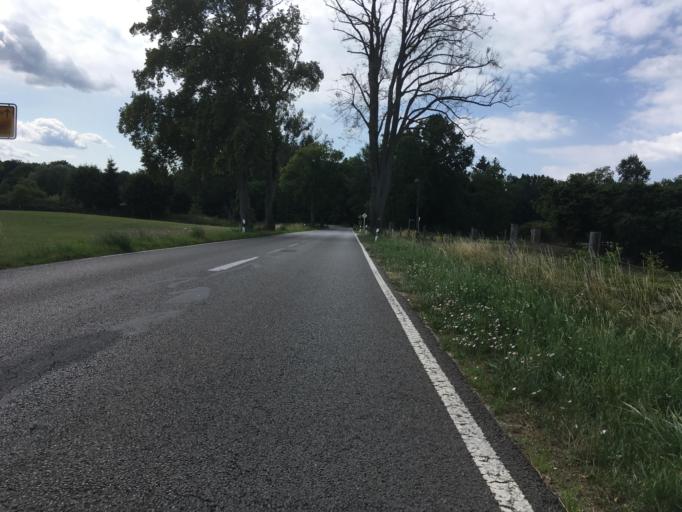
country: DE
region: Brandenburg
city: Friedrichswalde
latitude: 53.0551
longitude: 13.7144
